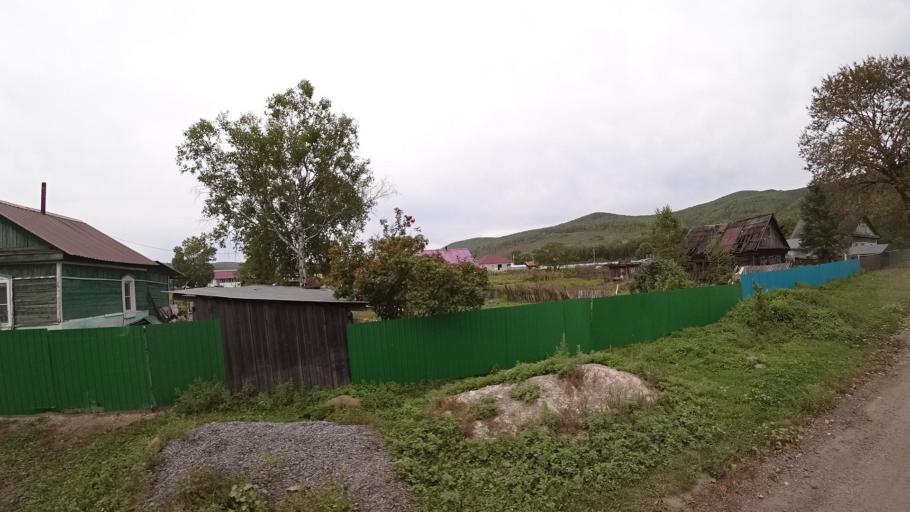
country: RU
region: Jewish Autonomous Oblast
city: Khingansk
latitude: 49.0339
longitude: 131.0506
